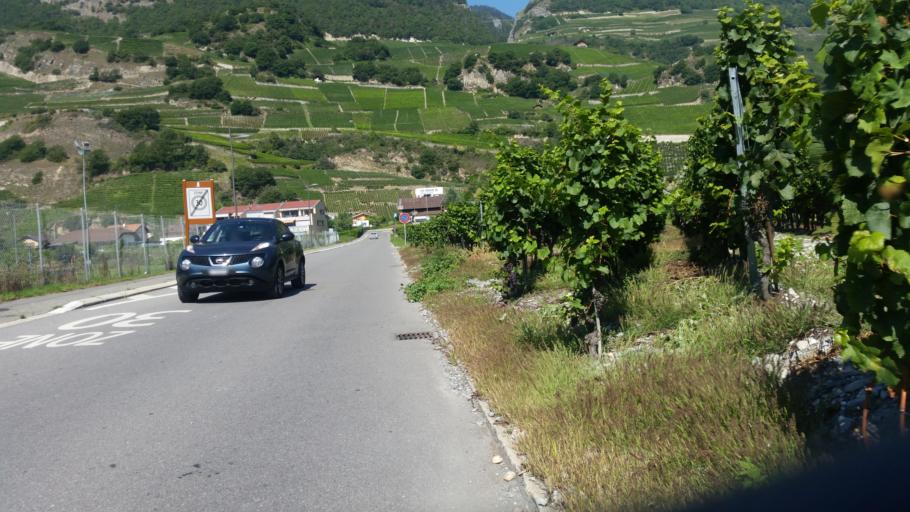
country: CH
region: Valais
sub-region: Martigny District
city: Saillon
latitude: 46.1750
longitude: 7.1942
